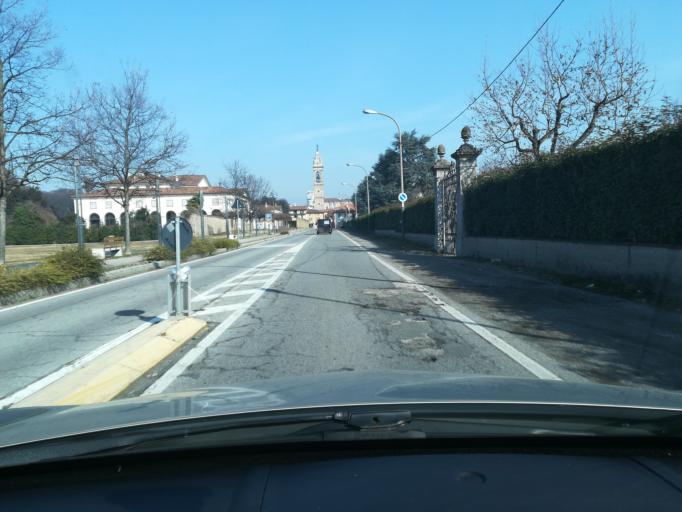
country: IT
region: Lombardy
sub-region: Provincia di Bergamo
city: Stezzano
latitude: 45.6464
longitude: 9.6507
